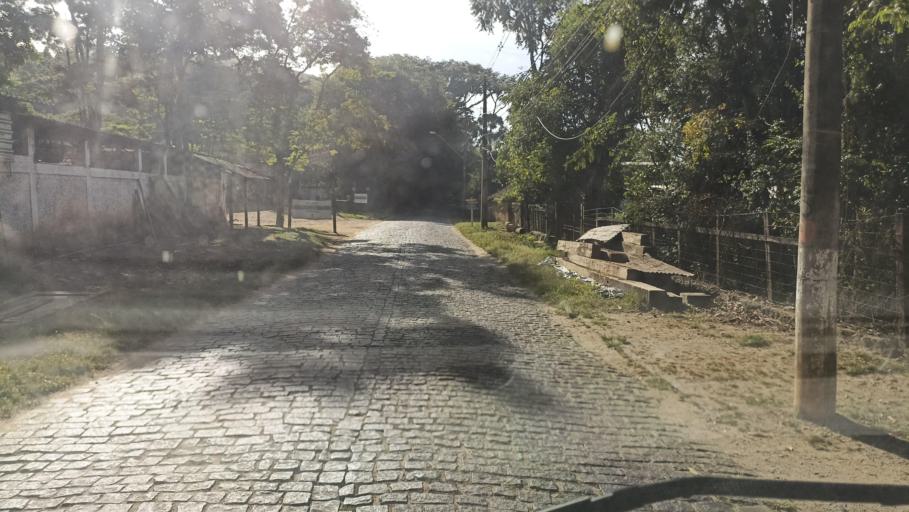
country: BR
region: Minas Gerais
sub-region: Tiradentes
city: Tiradentes
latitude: -21.1199
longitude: -44.1945
